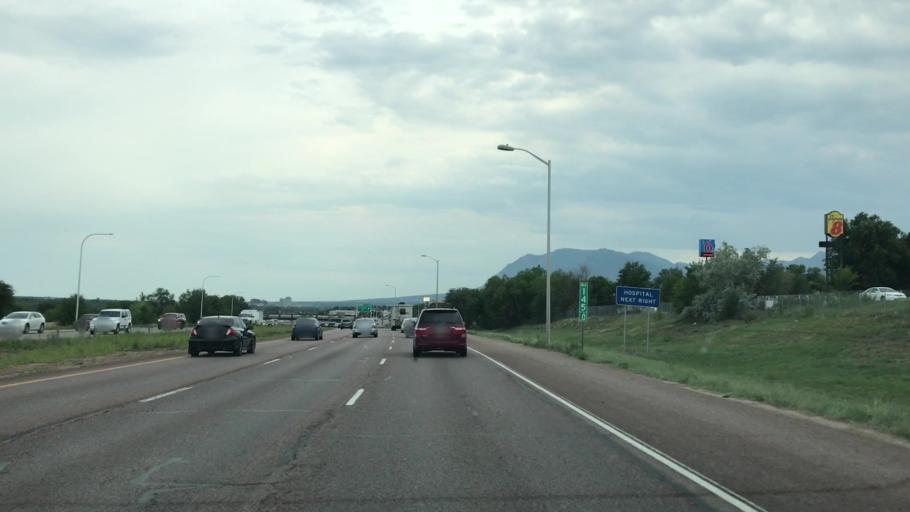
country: US
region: Colorado
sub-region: El Paso County
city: Colorado Springs
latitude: 38.8818
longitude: -104.8362
